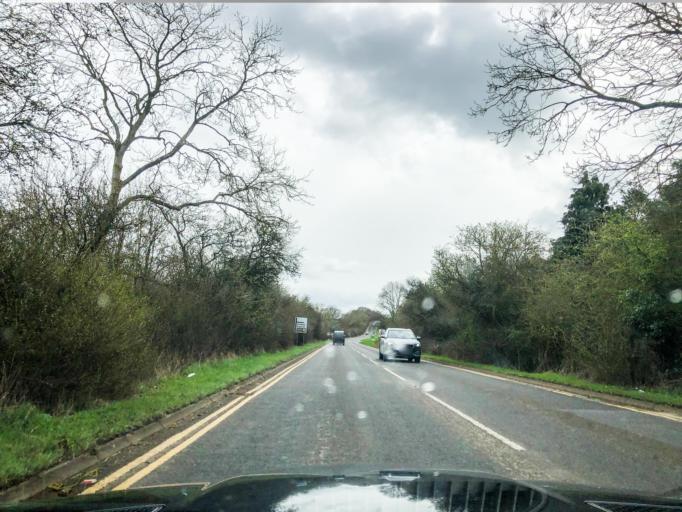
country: GB
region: England
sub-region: Warwickshire
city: Harbury
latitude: 52.1612
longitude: -1.4375
